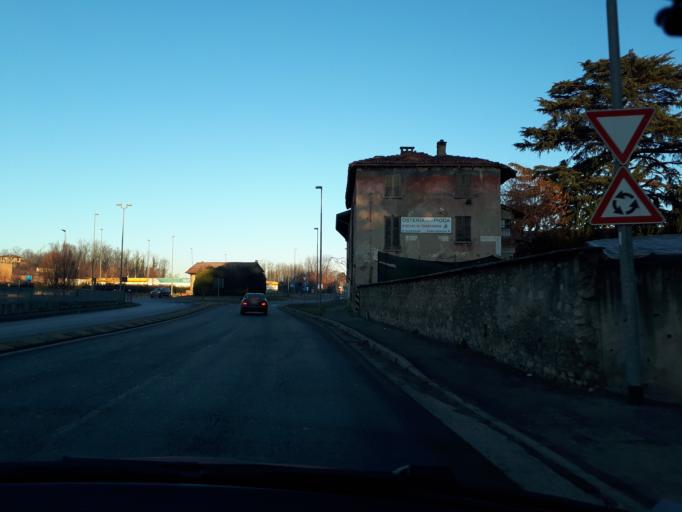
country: IT
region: Lombardy
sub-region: Provincia di Como
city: Vertemate Con Minoprio
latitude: 45.7254
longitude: 9.0679
